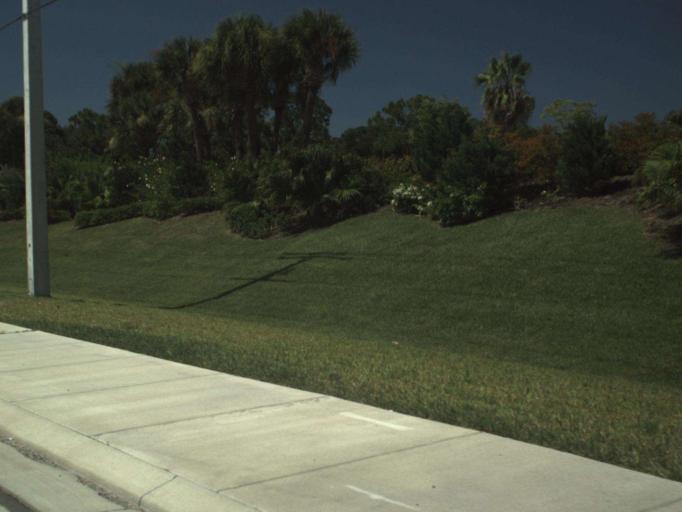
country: US
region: Florida
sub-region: Indian River County
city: Florida Ridge
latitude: 27.5786
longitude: -80.3754
